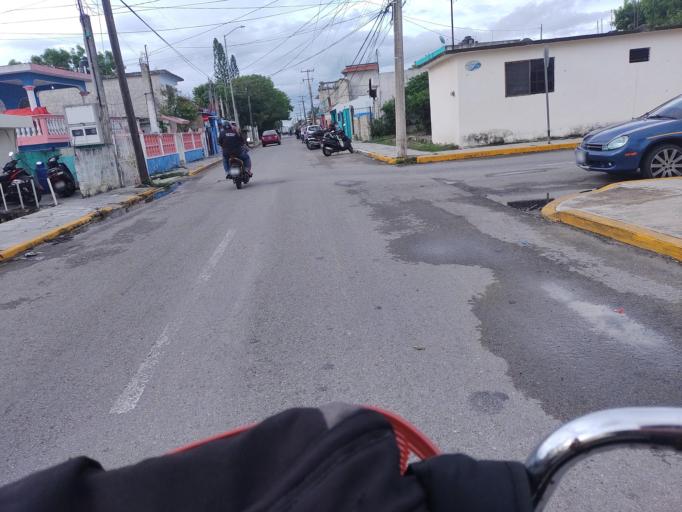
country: MX
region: Quintana Roo
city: San Miguel de Cozumel
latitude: 20.5035
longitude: -86.9512
